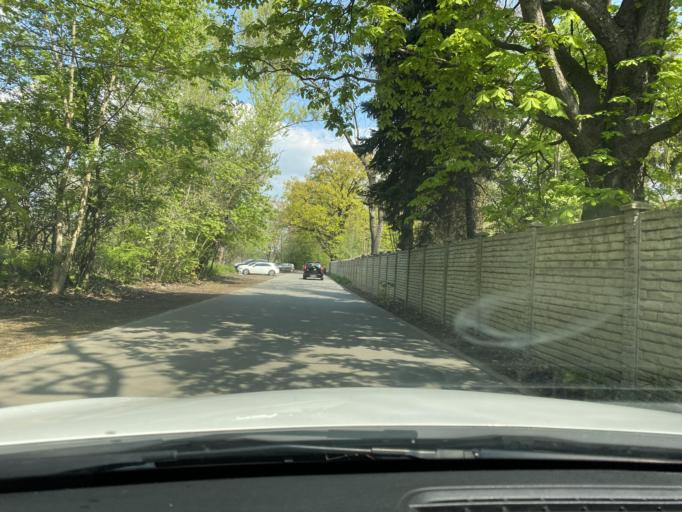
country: PL
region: Lower Silesian Voivodeship
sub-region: Powiat wroclawski
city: Wroclaw
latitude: 51.1393
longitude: 17.0059
